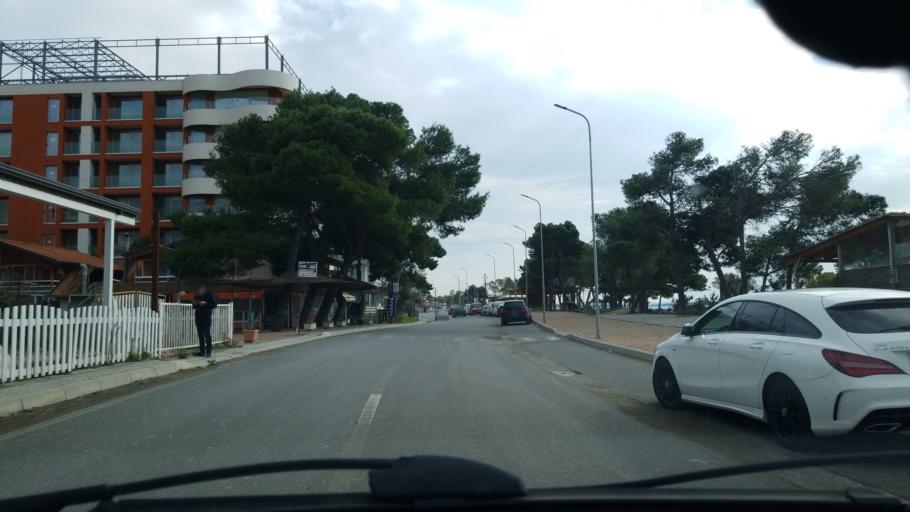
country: AL
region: Lezhe
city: Shengjin
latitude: 41.8006
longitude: 19.6011
